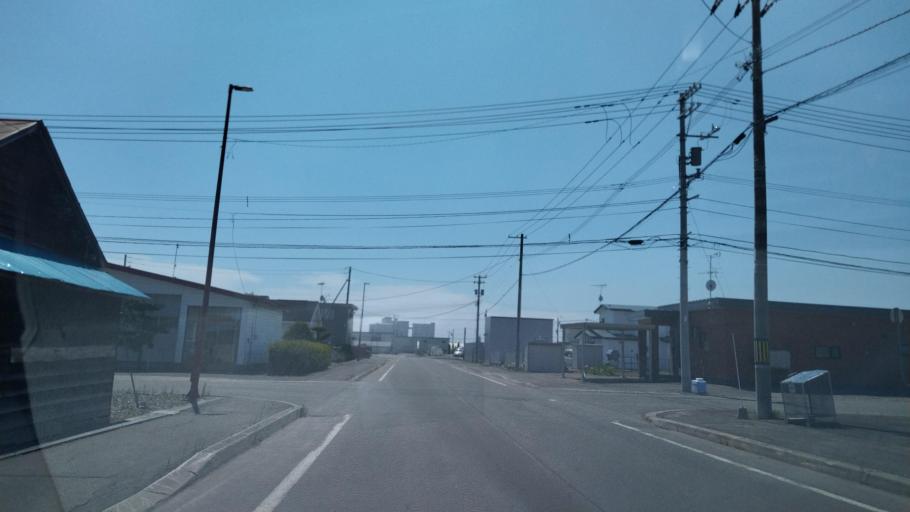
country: JP
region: Hokkaido
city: Otofuke
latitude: 43.1701
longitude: 143.2520
